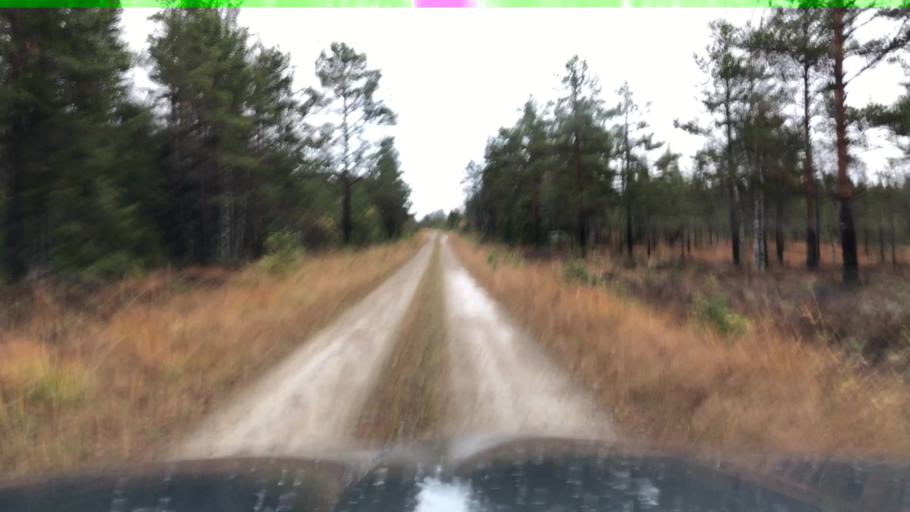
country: NO
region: Hedmark
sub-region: Trysil
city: Innbygda
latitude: 60.9278
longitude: 12.6450
